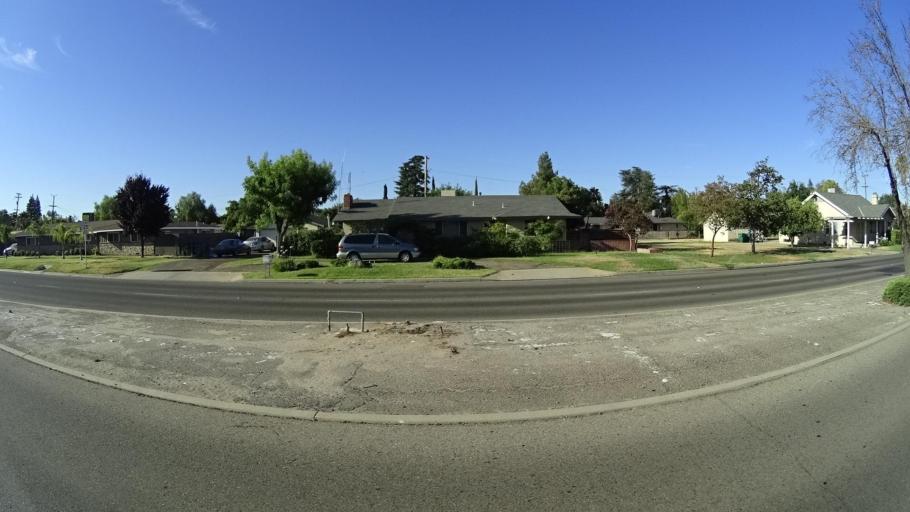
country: US
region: California
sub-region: Fresno County
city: Sunnyside
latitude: 36.7507
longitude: -119.7239
